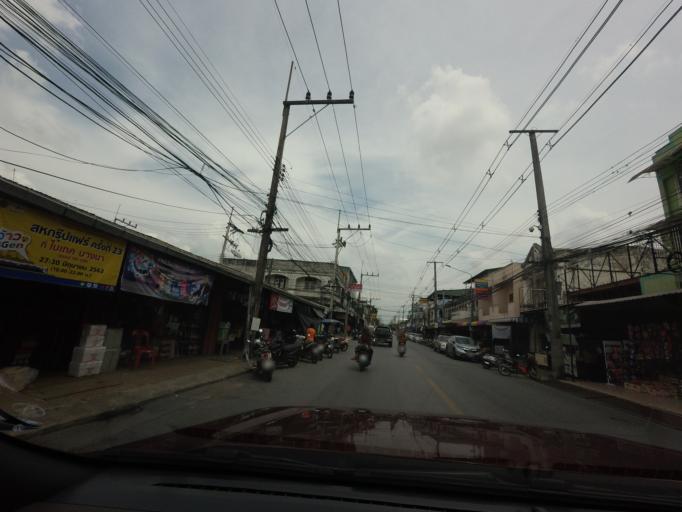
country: TH
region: Yala
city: Yala
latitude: 6.5499
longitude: 101.2937
